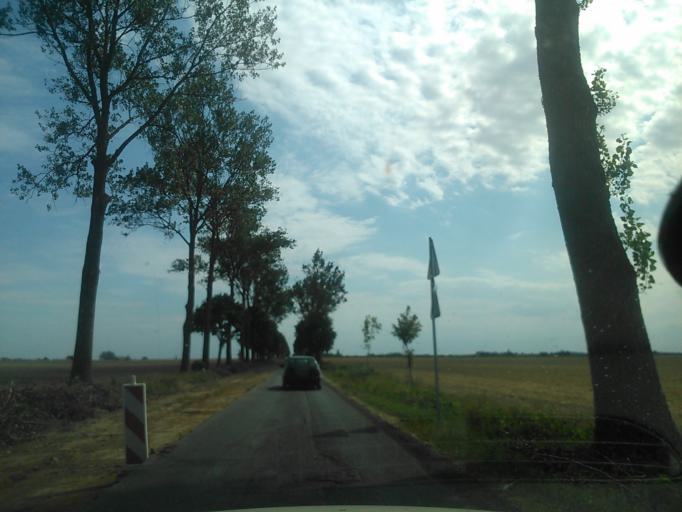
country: PL
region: Warmian-Masurian Voivodeship
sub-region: Powiat dzialdowski
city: Ilowo -Osada
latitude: 53.1870
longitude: 20.2827
